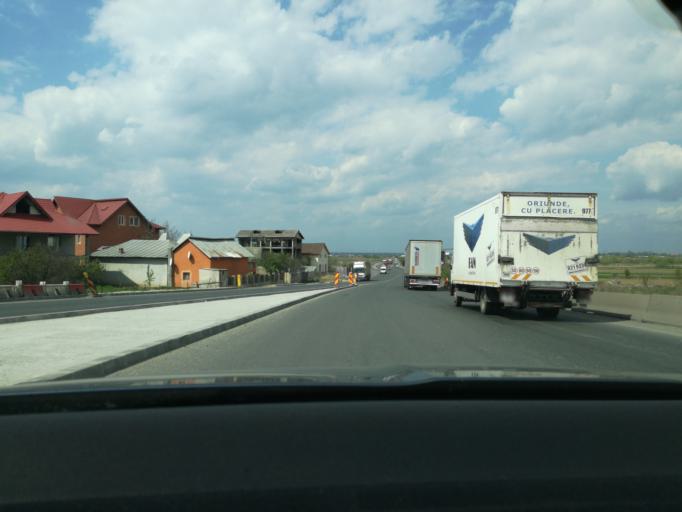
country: RO
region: Ilfov
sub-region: Comuna Dragomiresti-Vale
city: Dragomiresti-Deal
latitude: 44.4558
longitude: 25.9565
